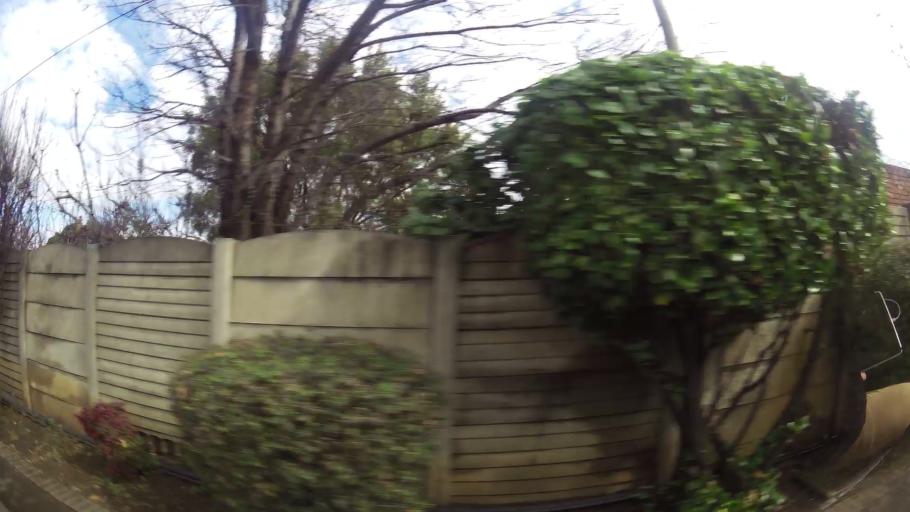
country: ZA
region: Gauteng
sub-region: Sedibeng District Municipality
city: Vereeniging
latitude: -26.6505
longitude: 27.9759
